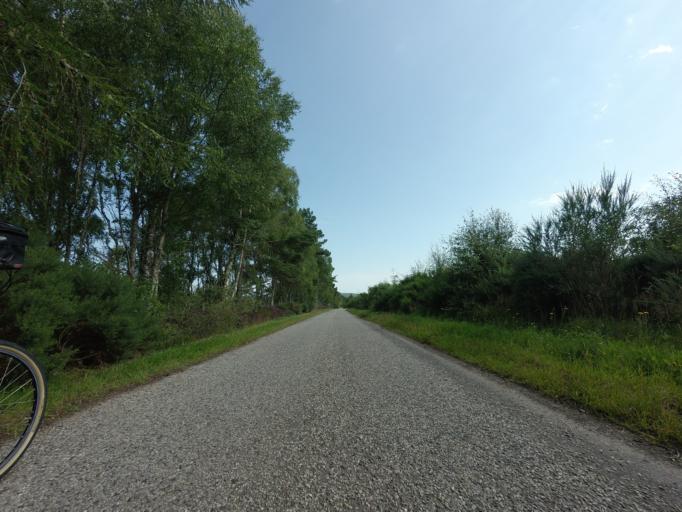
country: GB
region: Scotland
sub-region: Highland
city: Invergordon
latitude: 57.7370
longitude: -4.1875
